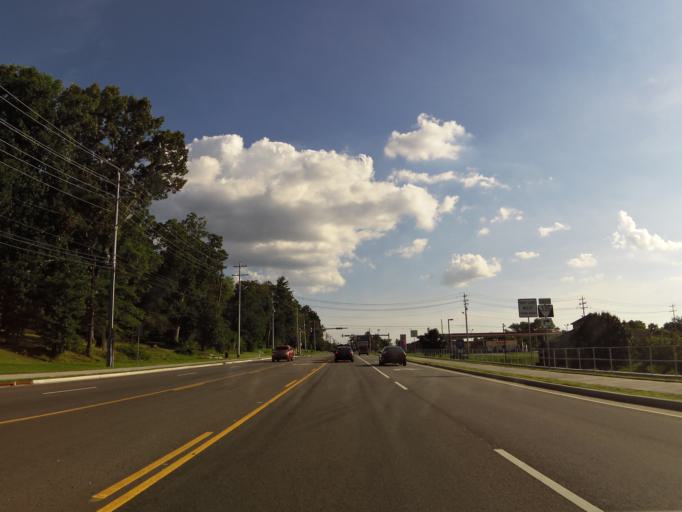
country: US
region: Tennessee
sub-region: Blount County
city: Eagleton Village
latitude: 35.8013
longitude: -83.9434
